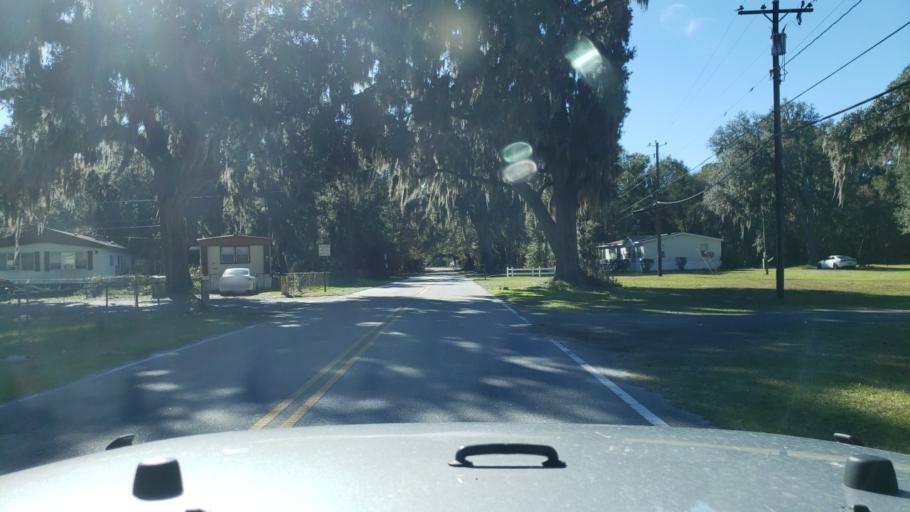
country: US
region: Georgia
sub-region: Chatham County
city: Georgetown
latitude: 32.0408
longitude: -81.1858
